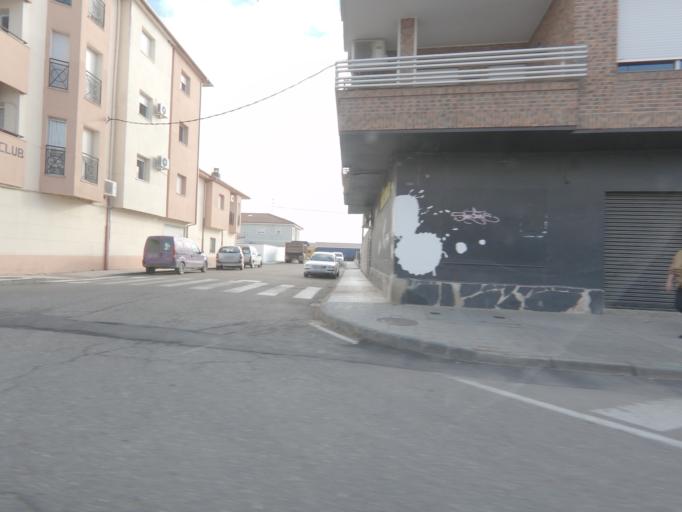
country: ES
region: Extremadura
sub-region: Provincia de Caceres
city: Moraleja
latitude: 40.0719
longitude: -6.6590
